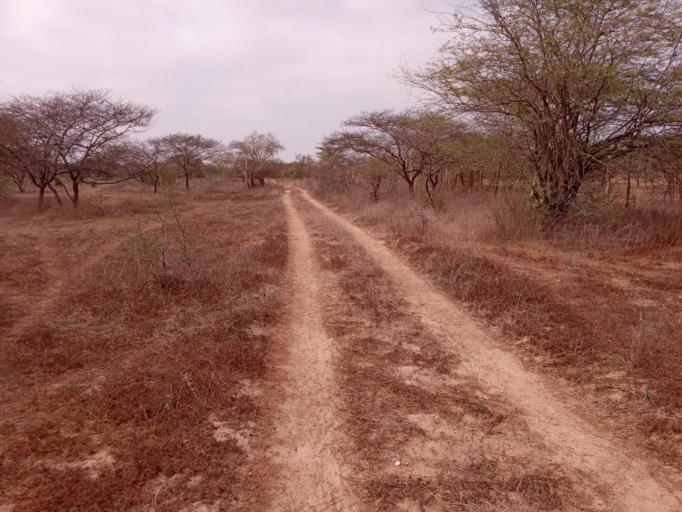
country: SN
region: Saint-Louis
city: Saint-Louis
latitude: 15.9145
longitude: -16.4544
